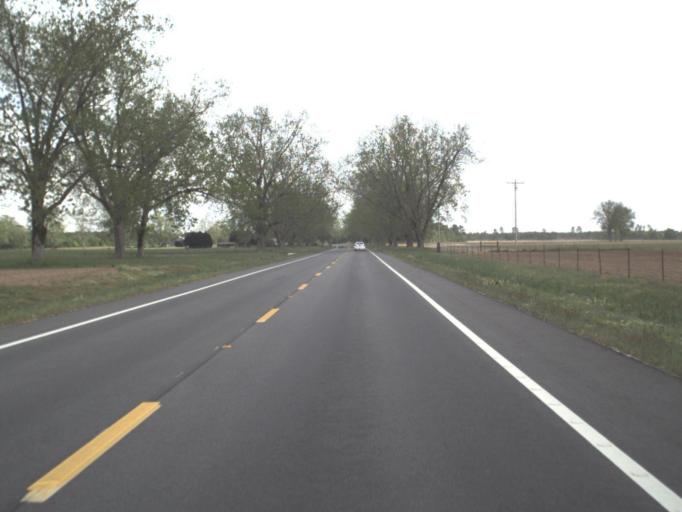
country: US
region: Florida
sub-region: Escambia County
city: Century
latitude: 30.8706
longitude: -87.1583
